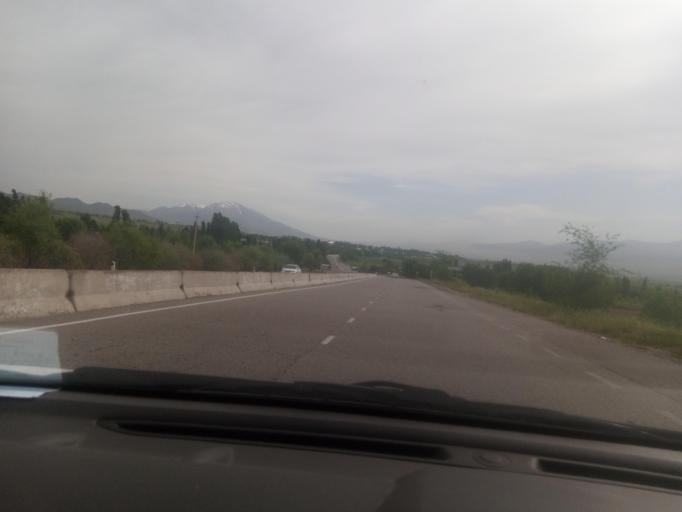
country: UZ
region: Toshkent
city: Angren
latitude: 40.9594
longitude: 69.9408
